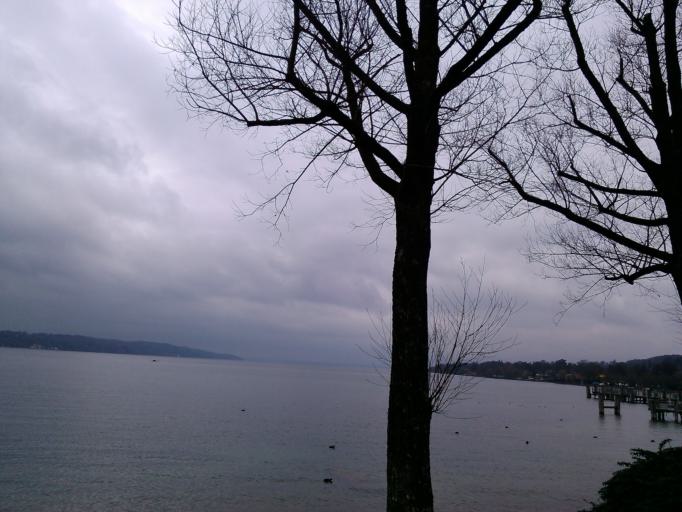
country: DE
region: Bavaria
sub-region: Upper Bavaria
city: Starnberg
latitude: 47.9959
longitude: 11.3444
